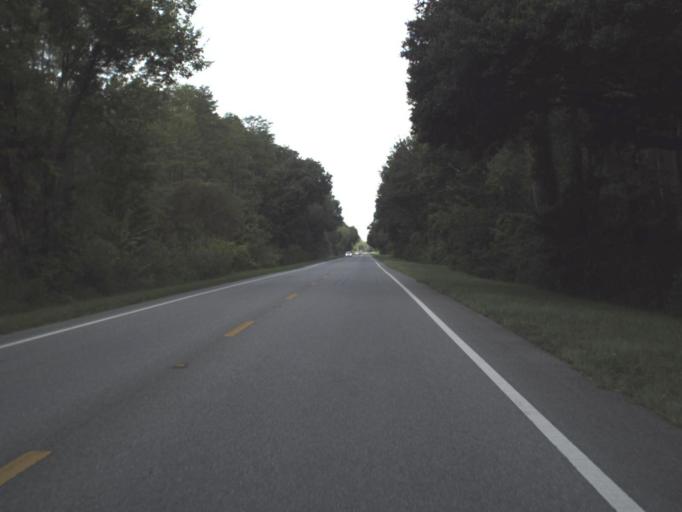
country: US
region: Florida
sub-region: Hernando County
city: Ridge Manor
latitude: 28.5077
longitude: -82.1315
